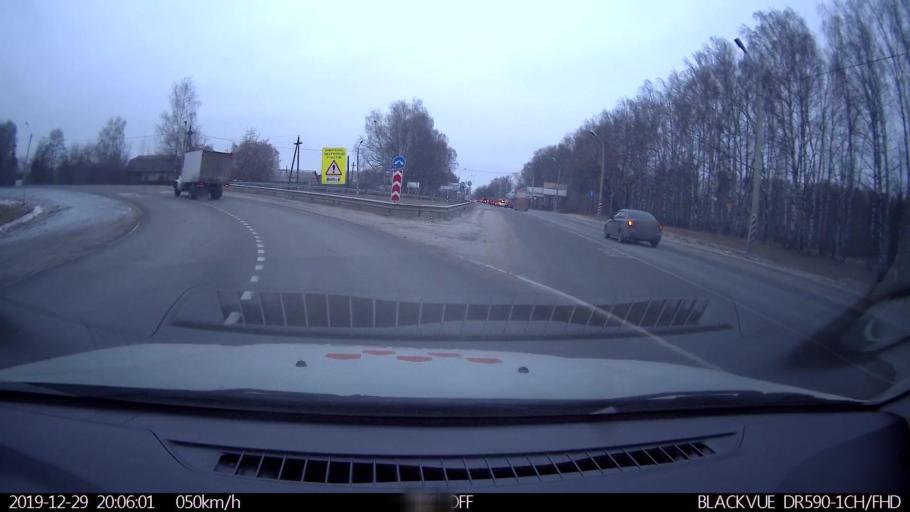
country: RU
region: Nizjnij Novgorod
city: Neklyudovo
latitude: 56.3945
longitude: 44.0090
